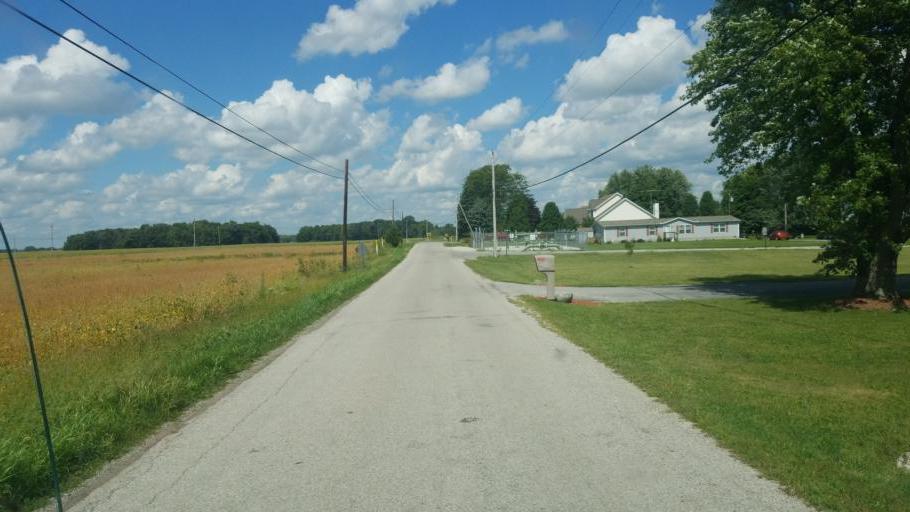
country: US
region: Ohio
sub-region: Marion County
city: Marion
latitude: 40.5329
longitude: -83.0981
